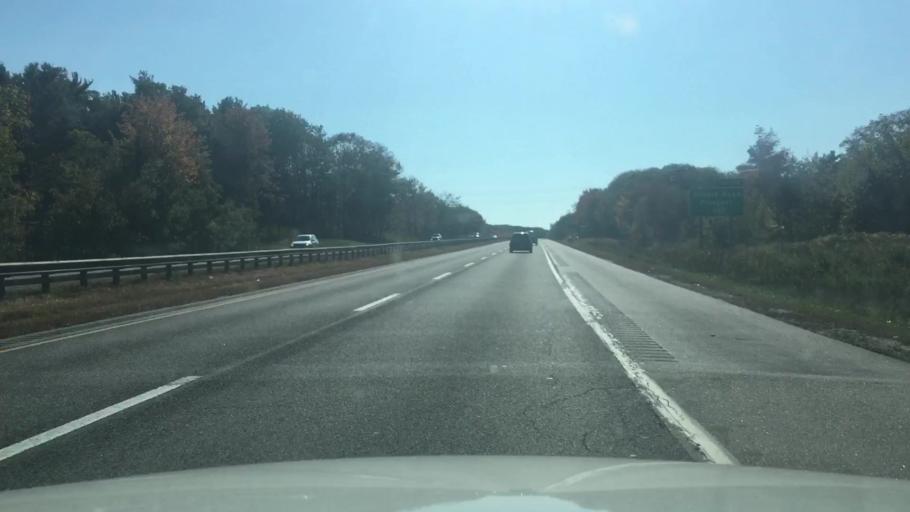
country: US
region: Maine
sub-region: Cumberland County
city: Freeport
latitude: 43.8588
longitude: -70.1116
